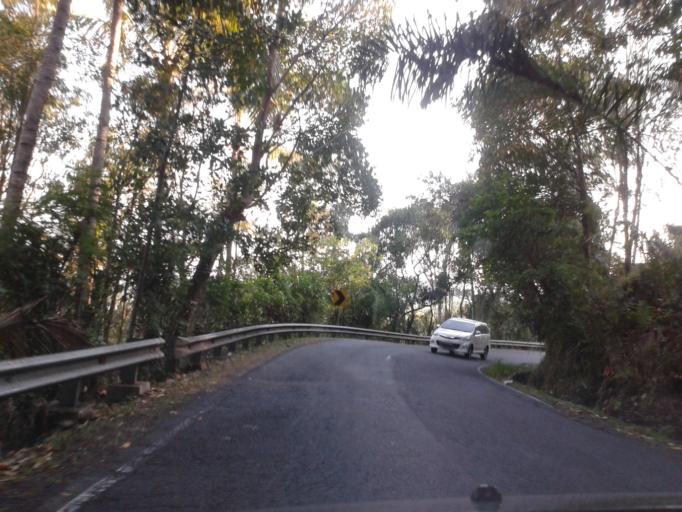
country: ID
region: Bali
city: Banjar Wangsian
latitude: -8.4799
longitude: 115.4006
